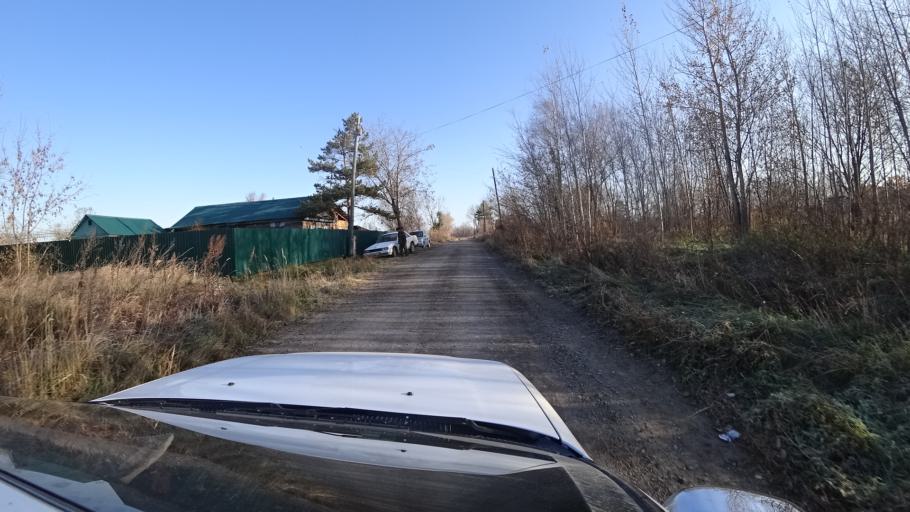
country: RU
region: Primorskiy
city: Lazo
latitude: 45.8743
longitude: 133.6462
